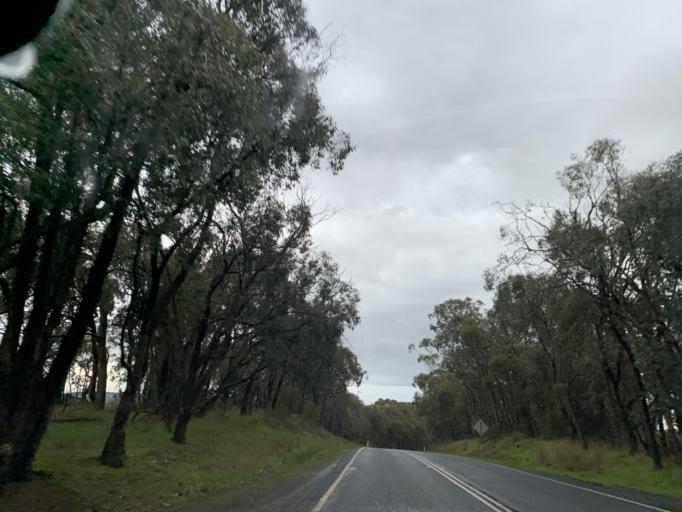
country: AU
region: Victoria
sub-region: Murrindindi
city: Kinglake West
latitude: -37.2197
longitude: 145.1318
